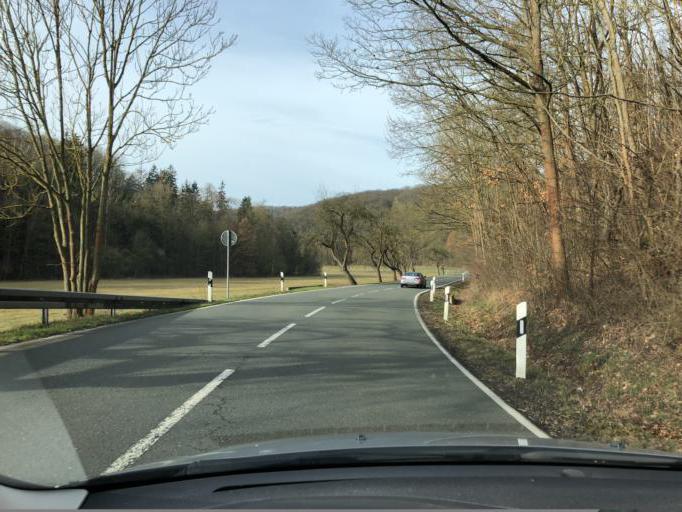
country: DE
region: Saxony-Anhalt
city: Laucha
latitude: 51.2339
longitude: 11.6314
